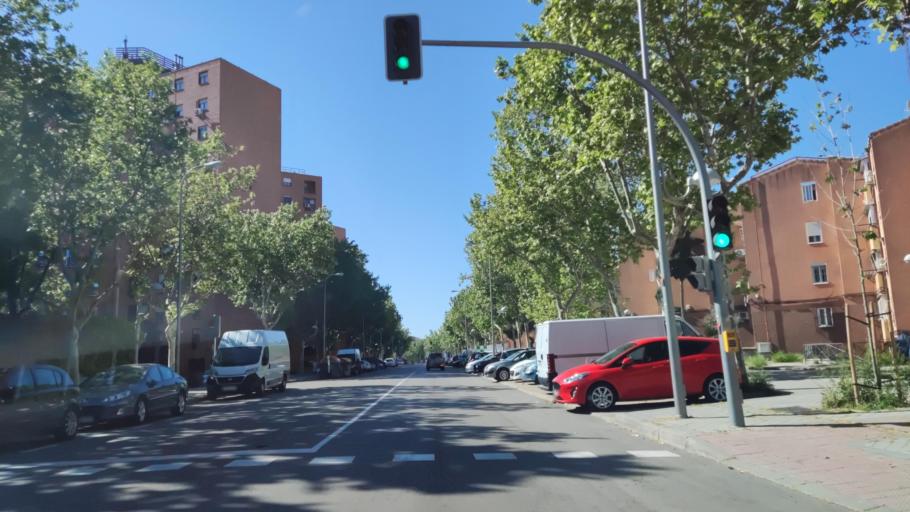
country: ES
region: Madrid
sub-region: Provincia de Madrid
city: San Blas
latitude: 40.4319
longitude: -3.6161
